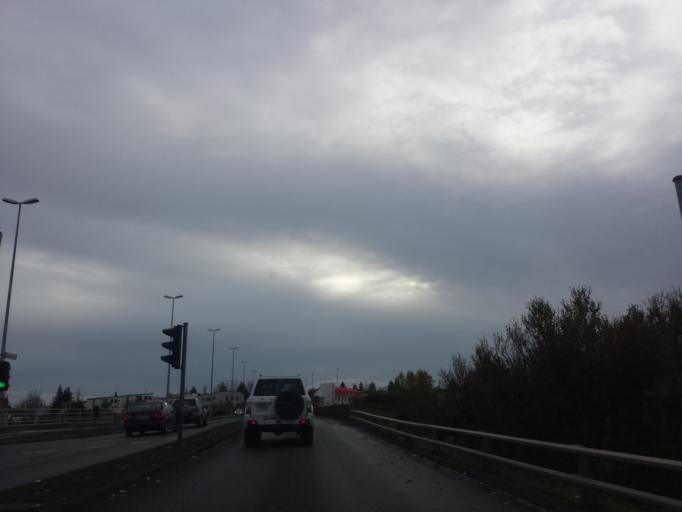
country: IS
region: Capital Region
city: Reykjavik
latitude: 64.1282
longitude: -21.8631
